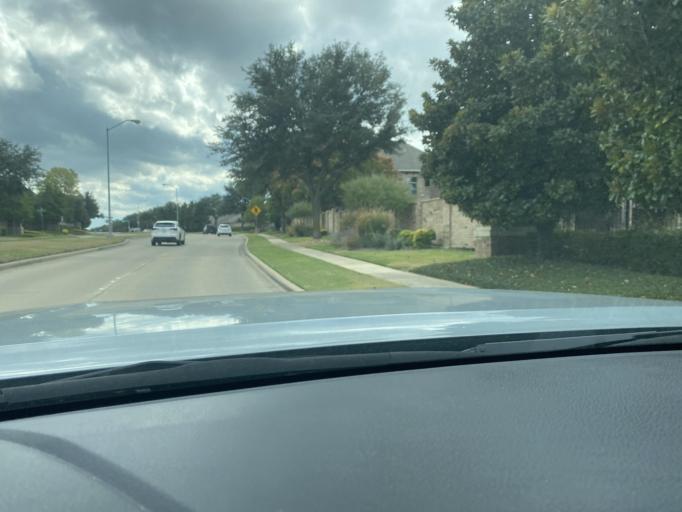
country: US
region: Texas
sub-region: Dallas County
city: Addison
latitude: 33.0379
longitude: -96.7896
